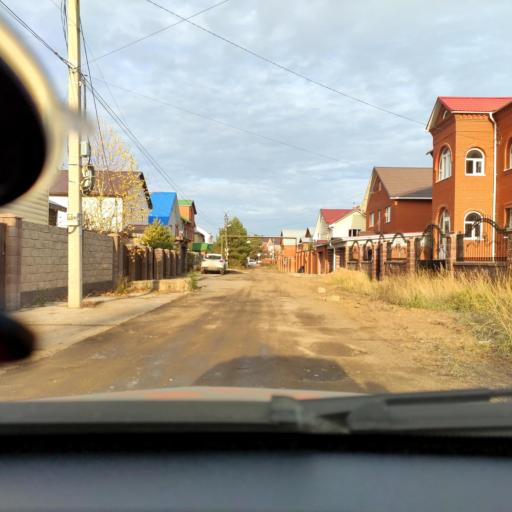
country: RU
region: Bashkortostan
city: Ufa
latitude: 54.7922
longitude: 55.9483
